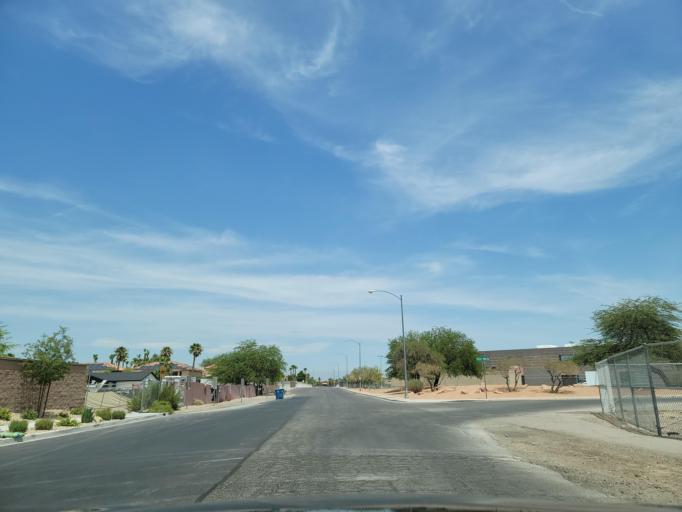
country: US
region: Nevada
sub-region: Clark County
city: Whitney
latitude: 36.0221
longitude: -115.1319
